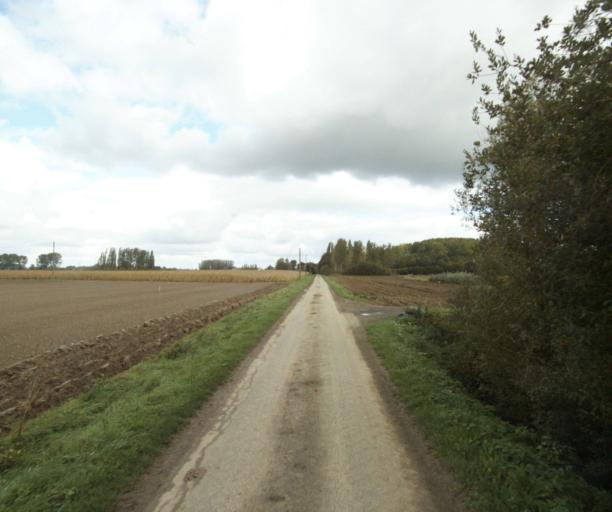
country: FR
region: Nord-Pas-de-Calais
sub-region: Departement du Nord
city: Frelinghien
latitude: 50.6984
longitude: 2.9455
